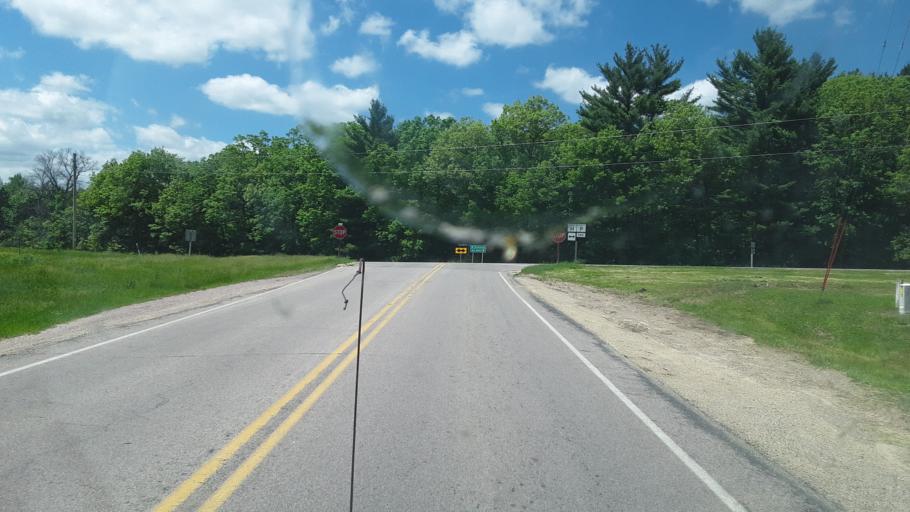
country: US
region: Wisconsin
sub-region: Sauk County
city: Reedsburg
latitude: 43.5923
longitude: -89.9095
